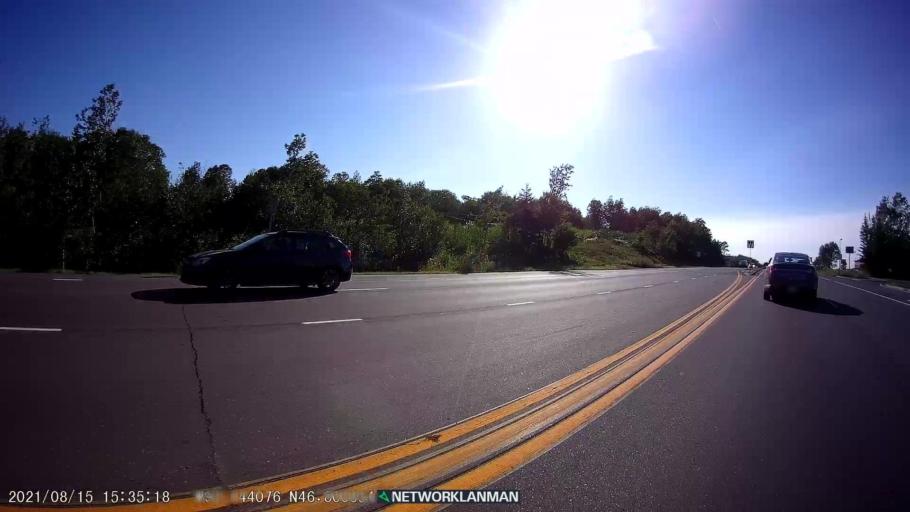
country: US
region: Minnesota
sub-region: Saint Louis County
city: Duluth
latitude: 46.8009
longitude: -92.1440
